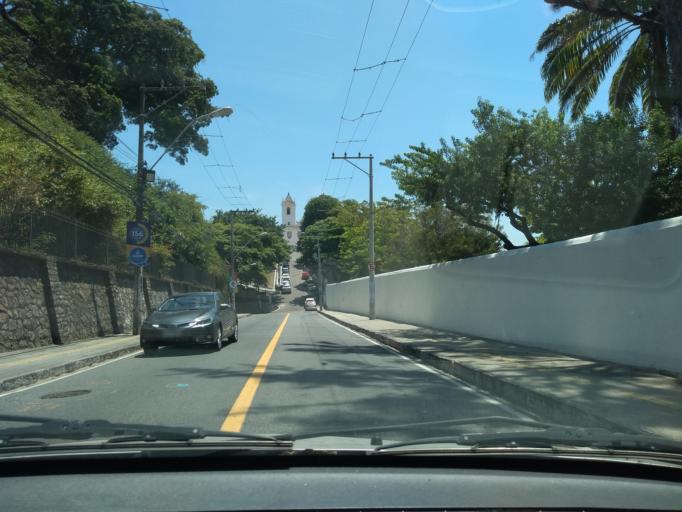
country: BR
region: Bahia
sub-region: Salvador
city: Salvador
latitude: -13.0005
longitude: -38.5308
